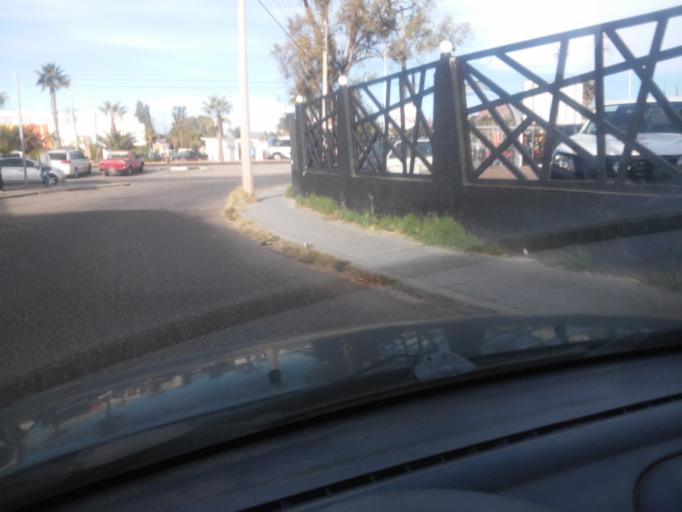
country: MX
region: Durango
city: Victoria de Durango
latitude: 24.0409
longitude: -104.6574
